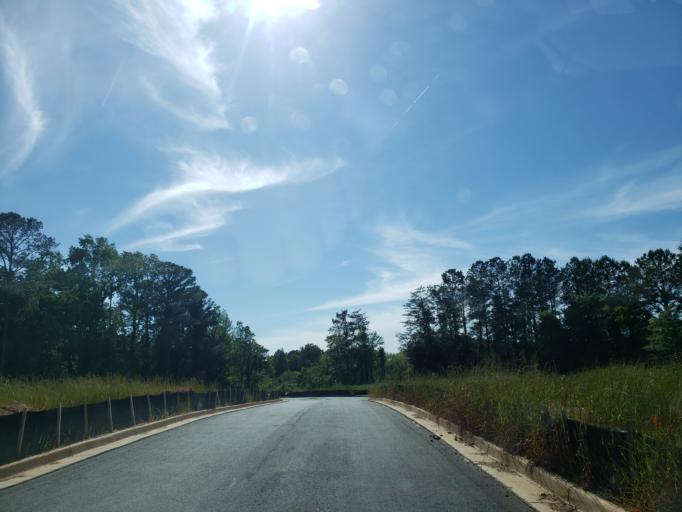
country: US
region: Georgia
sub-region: Fulton County
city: Sandy Springs
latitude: 33.9749
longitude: -84.4169
